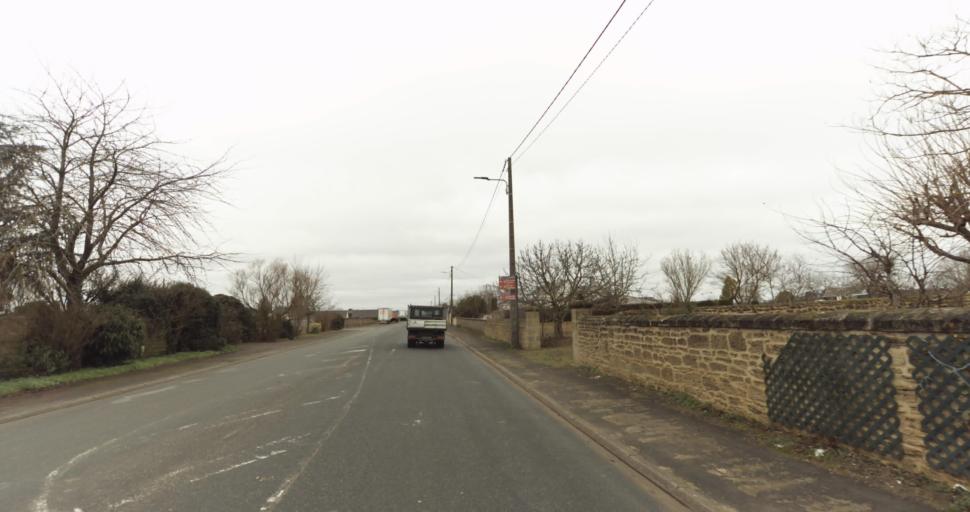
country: FR
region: Pays de la Loire
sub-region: Departement de Maine-et-Loire
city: Doue-la-Fontaine
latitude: 47.1844
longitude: -0.2519
